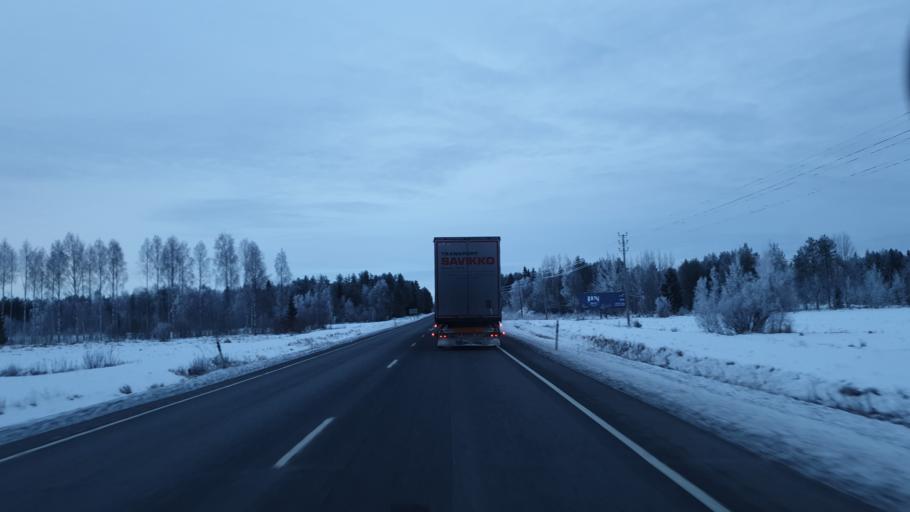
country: FI
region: Northern Ostrobothnia
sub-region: Oulunkaari
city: Ii
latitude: 65.3526
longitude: 25.3709
